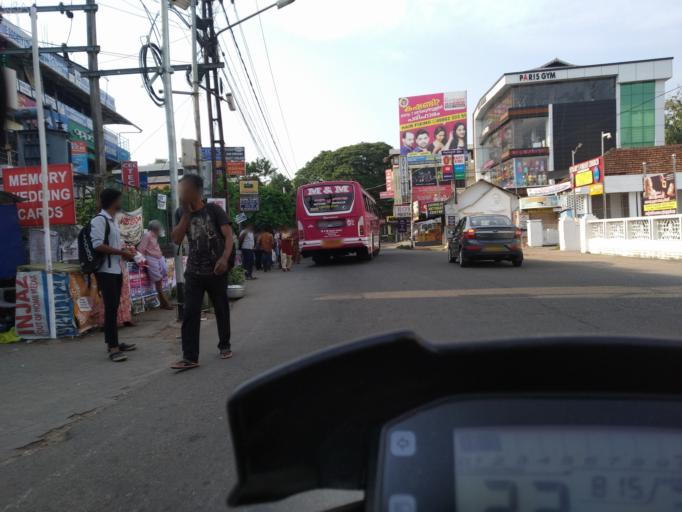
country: IN
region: Kerala
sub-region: Alappuzha
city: Arukutti
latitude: 9.9449
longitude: 76.3489
